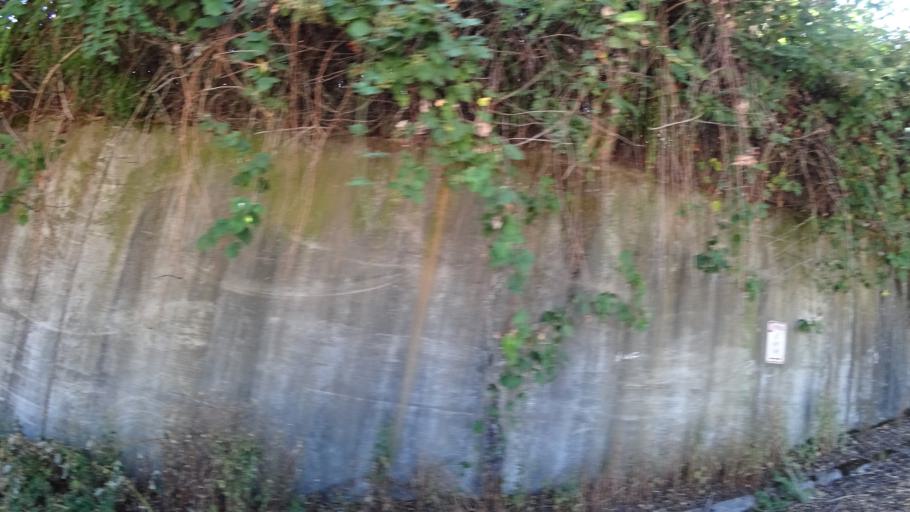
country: US
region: Oregon
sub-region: Multnomah County
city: Portland
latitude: 45.4862
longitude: -122.6788
